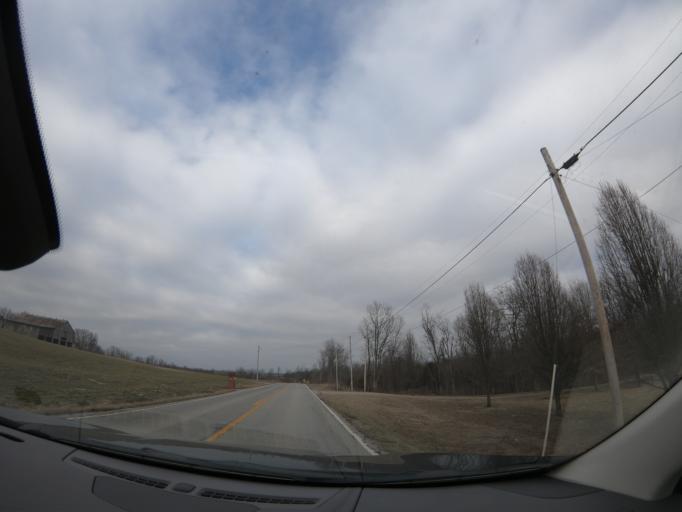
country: US
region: Kentucky
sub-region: Spencer County
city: Taylorsville
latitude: 37.8766
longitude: -85.3074
